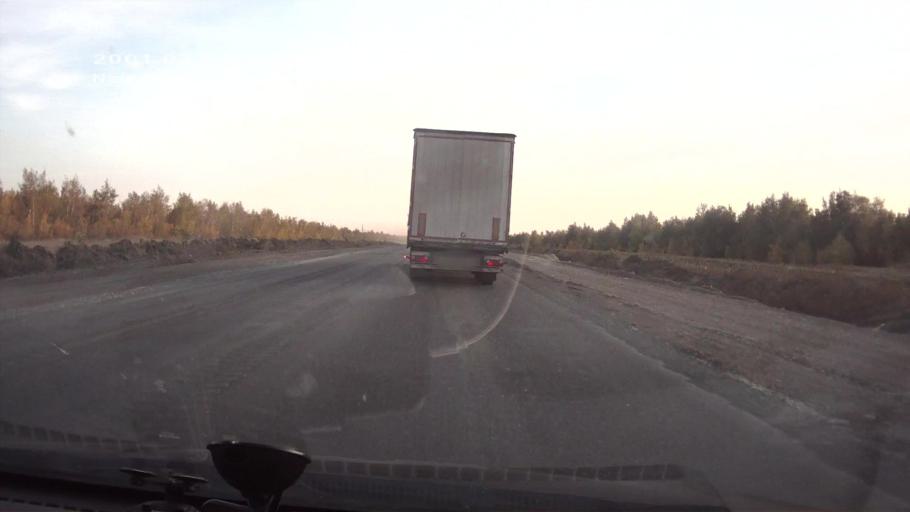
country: RU
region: Saratov
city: Kamenskiy
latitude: 50.9306
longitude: 45.5999
